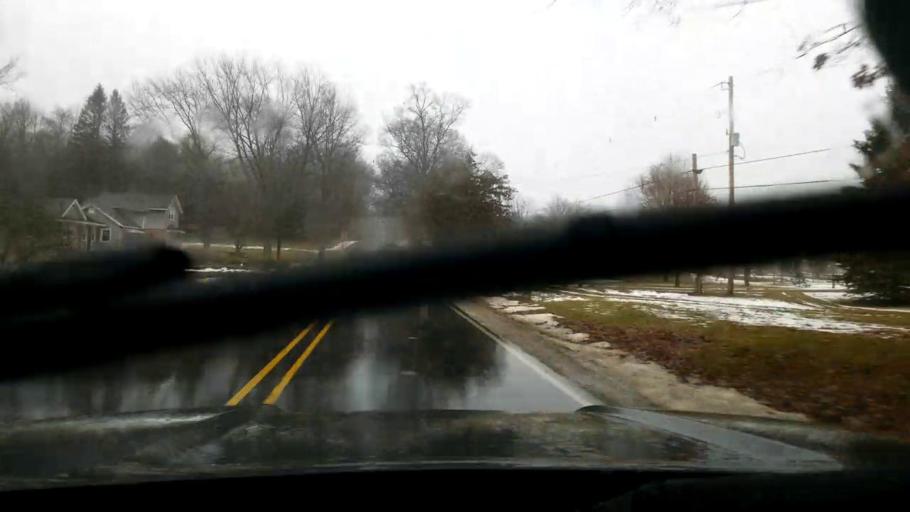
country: US
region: Michigan
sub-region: Jackson County
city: Grass Lake
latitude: 42.3212
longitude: -84.2698
